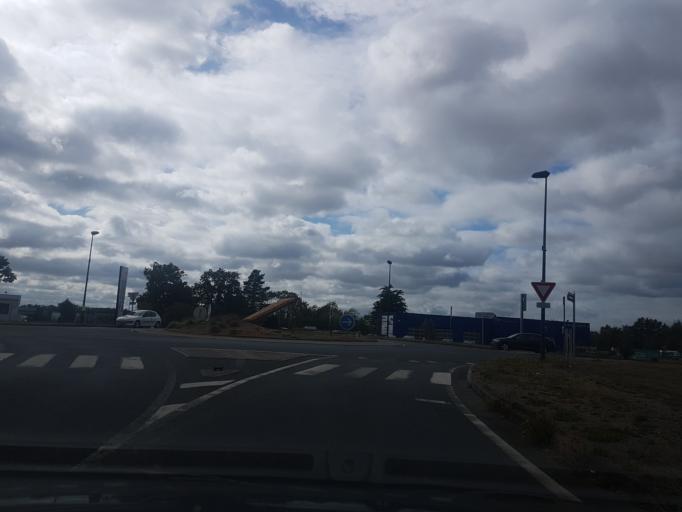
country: FR
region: Pays de la Loire
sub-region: Departement de la Loire-Atlantique
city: Ligne
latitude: 47.4138
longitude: -1.3915
